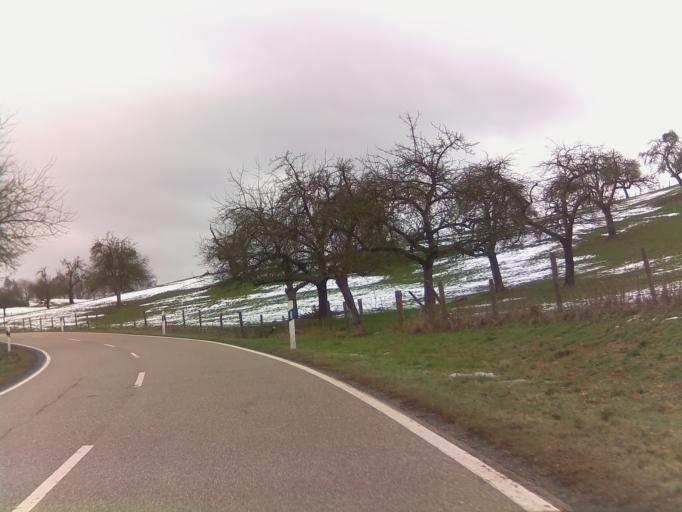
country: DE
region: Hesse
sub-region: Regierungsbezirk Darmstadt
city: Erbach
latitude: 49.6807
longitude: 8.9489
